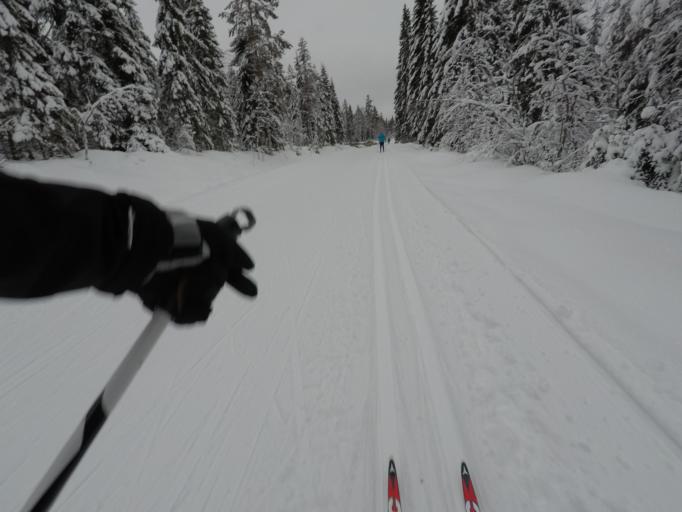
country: SE
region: Dalarna
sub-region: Ludvika Kommun
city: Abborrberget
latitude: 60.1560
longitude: 14.4895
